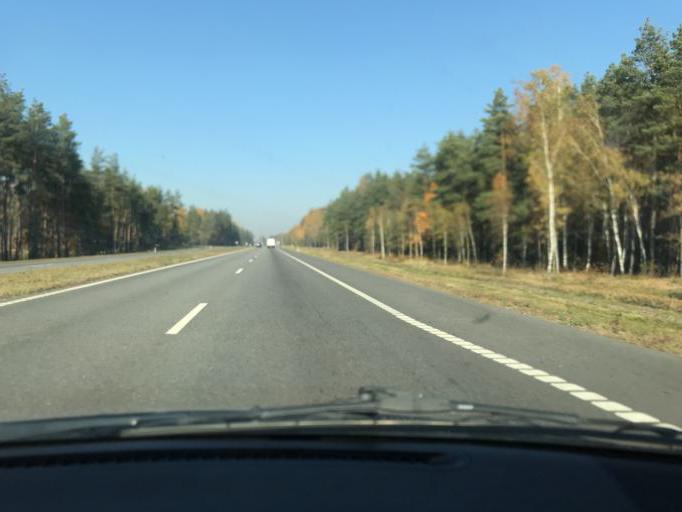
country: BY
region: Minsk
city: Slutsk
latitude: 53.3272
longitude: 27.5319
